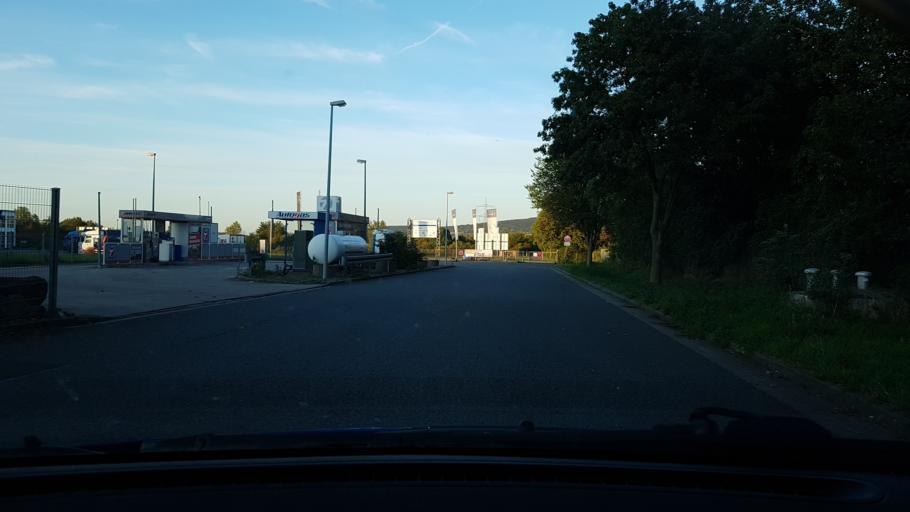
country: DE
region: Lower Saxony
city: Pohle
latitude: 52.2776
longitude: 9.3478
